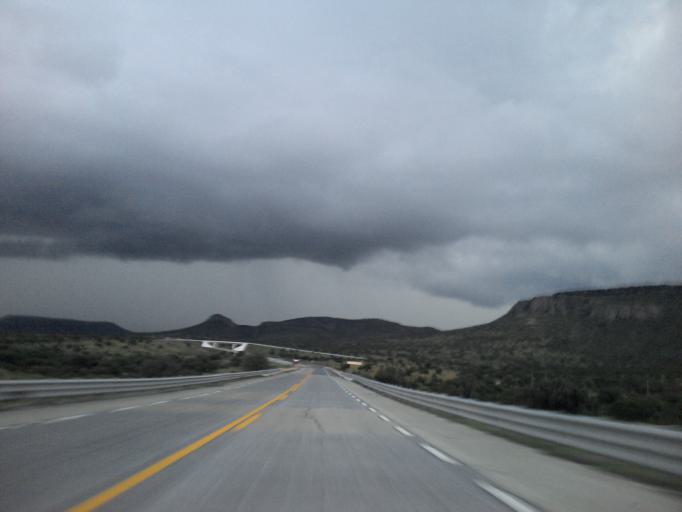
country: MX
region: Zacatecas
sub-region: Cuauhtemoc
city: Piedra Gorda
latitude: 22.5971
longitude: -102.4030
